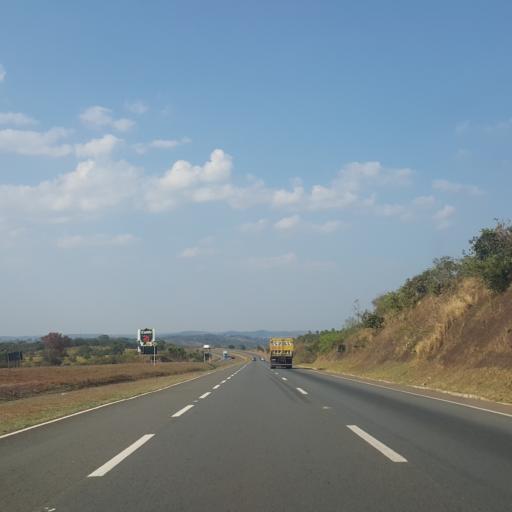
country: BR
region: Goias
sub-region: Abadiania
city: Abadiania
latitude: -16.1854
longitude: -48.6595
